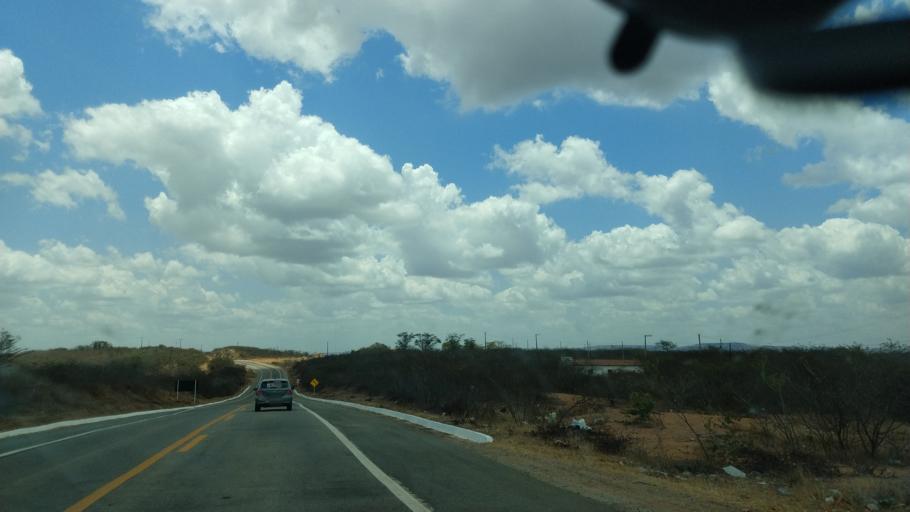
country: BR
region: Rio Grande do Norte
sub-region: Cerro Cora
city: Cerro Cora
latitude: -6.1884
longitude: -36.2335
